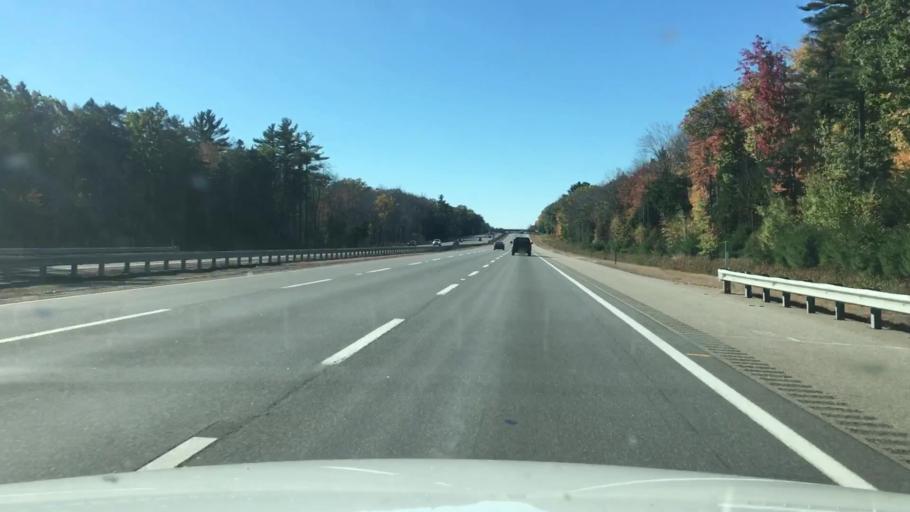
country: US
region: Maine
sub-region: York County
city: Wells Beach Station
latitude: 43.3423
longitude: -70.5978
